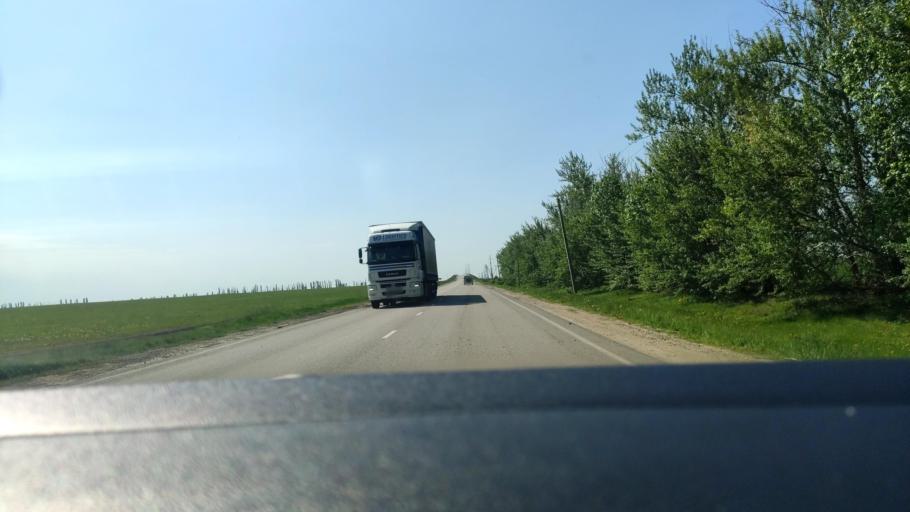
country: RU
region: Voronezj
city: Novaya Usman'
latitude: 51.5990
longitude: 39.3735
